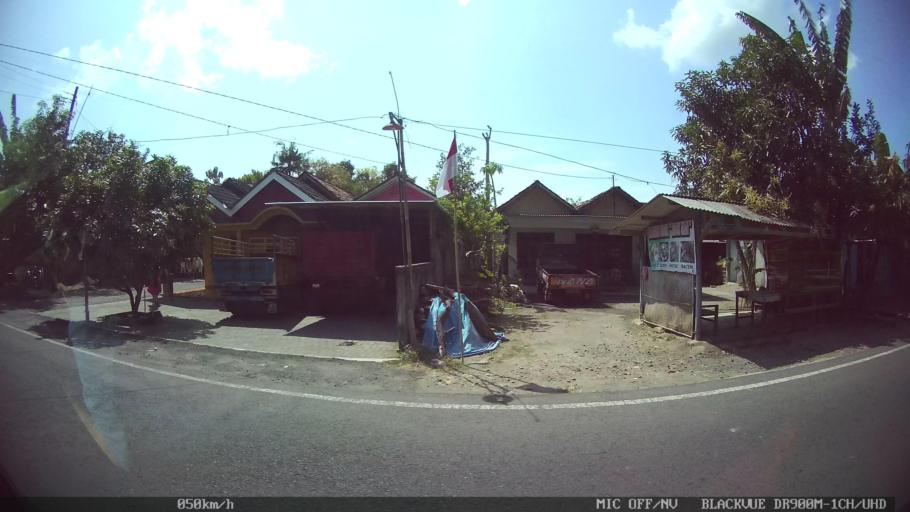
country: ID
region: Daerah Istimewa Yogyakarta
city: Pundong
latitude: -7.9881
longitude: 110.3208
